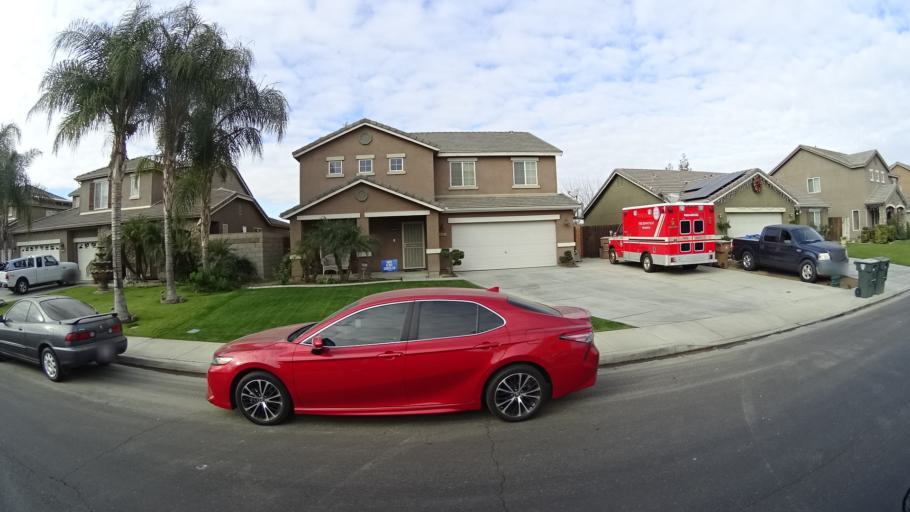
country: US
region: California
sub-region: Kern County
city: Rosedale
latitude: 35.3009
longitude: -119.1318
